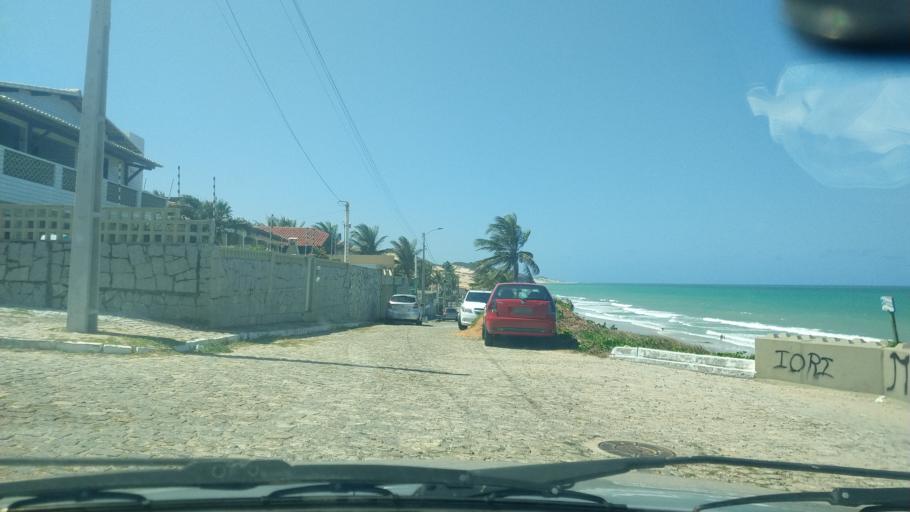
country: BR
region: Rio Grande do Norte
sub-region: Parnamirim
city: Parnamirim
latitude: -5.9499
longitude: -35.1531
